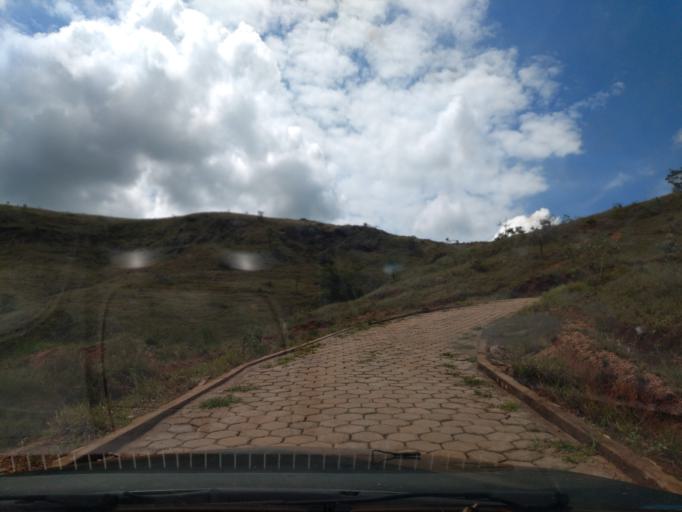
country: BR
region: Minas Gerais
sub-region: Lavras
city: Lavras
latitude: -21.5204
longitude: -44.9305
